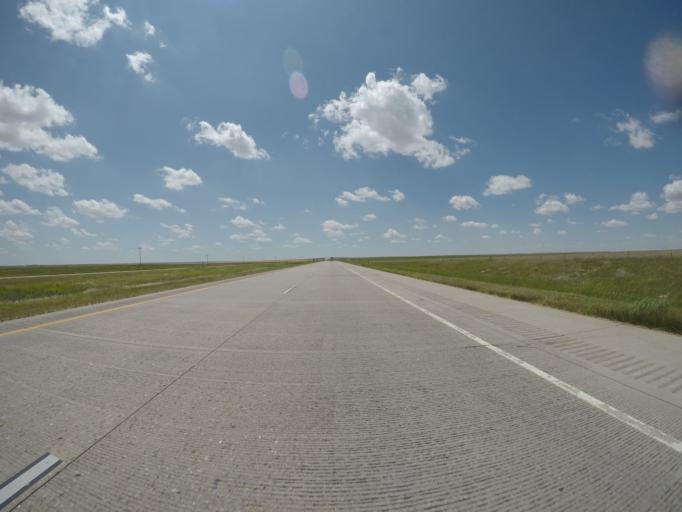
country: US
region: Colorado
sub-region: Lincoln County
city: Hugo
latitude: 39.2816
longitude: -102.9453
